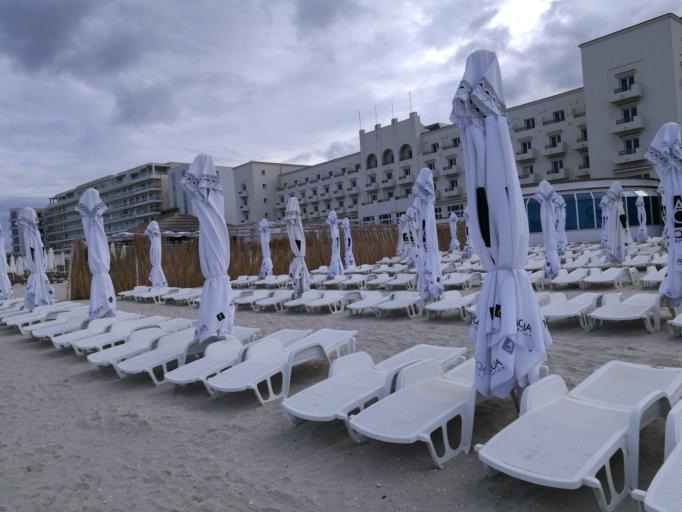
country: RO
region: Constanta
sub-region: Municipiul Constanta
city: Palazu Mare
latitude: 44.2486
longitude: 28.6231
